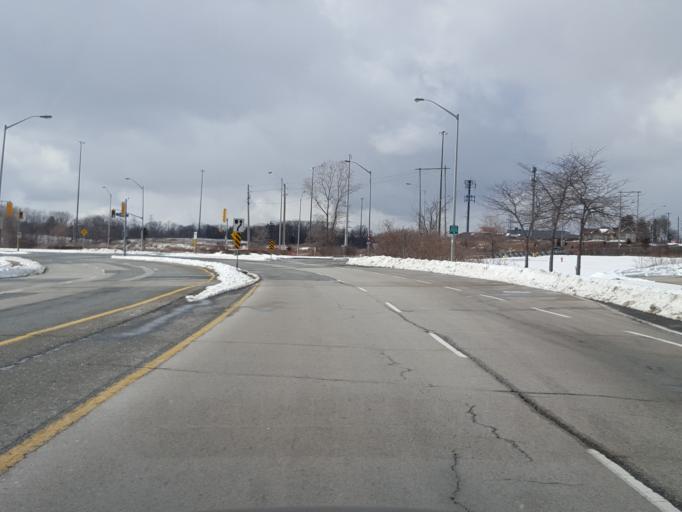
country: CA
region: Ontario
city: Hamilton
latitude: 43.2935
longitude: -79.8877
